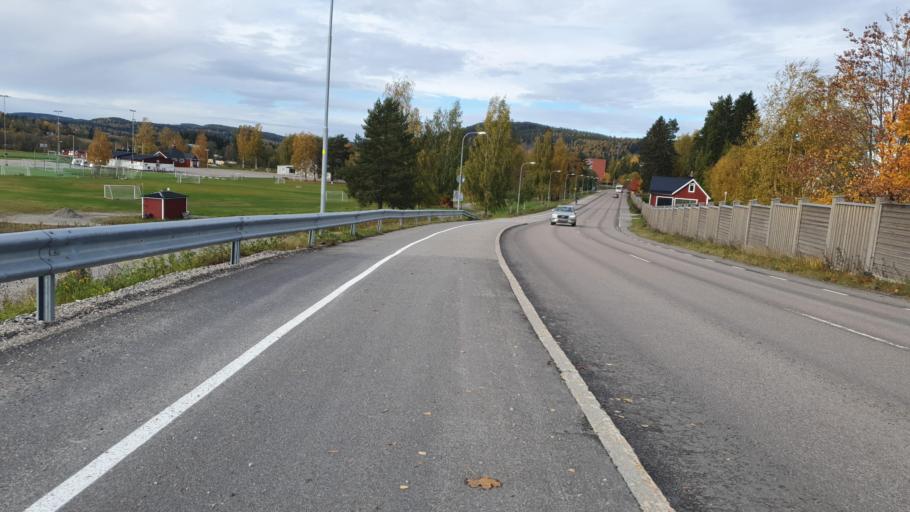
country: SE
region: Vaesternorrland
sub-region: Sundsvalls Kommun
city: Sundsvall
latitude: 62.4084
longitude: 17.2316
